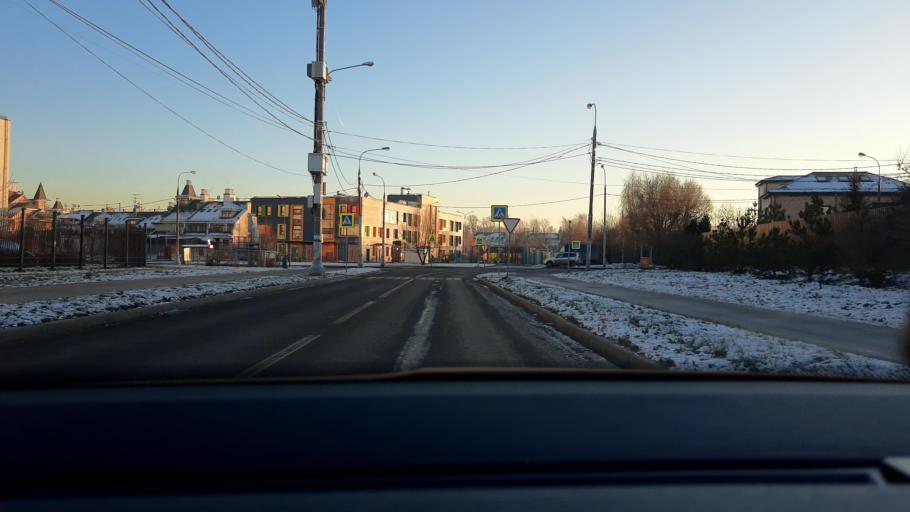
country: RU
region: Moskovskaya
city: Novopodrezkovo
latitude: 55.8998
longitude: 37.3761
